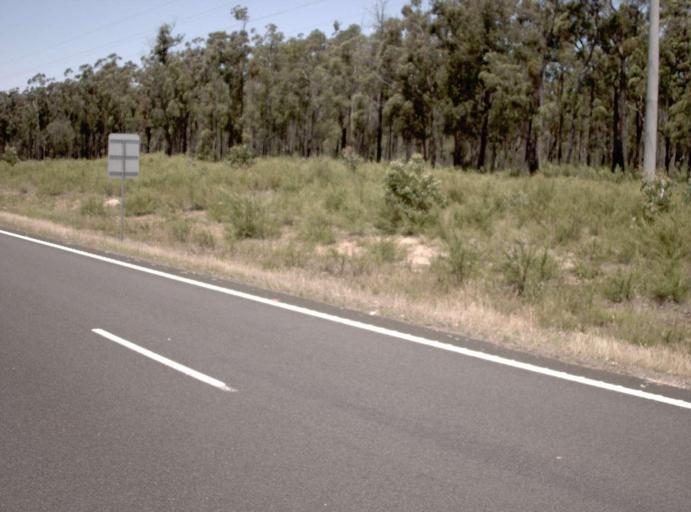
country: AU
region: Victoria
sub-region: East Gippsland
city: Lakes Entrance
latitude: -37.7340
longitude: 148.1448
